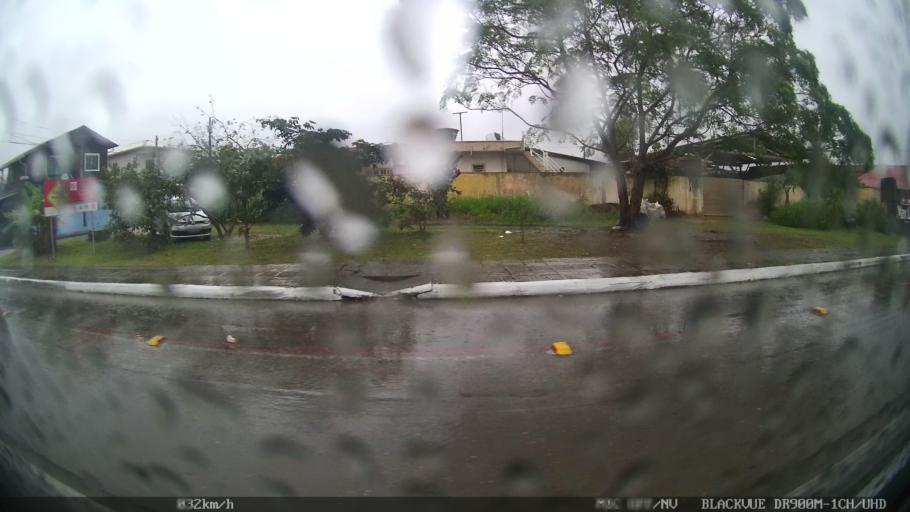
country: BR
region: Santa Catarina
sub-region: Navegantes
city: Navegantes
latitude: -26.8866
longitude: -48.6616
